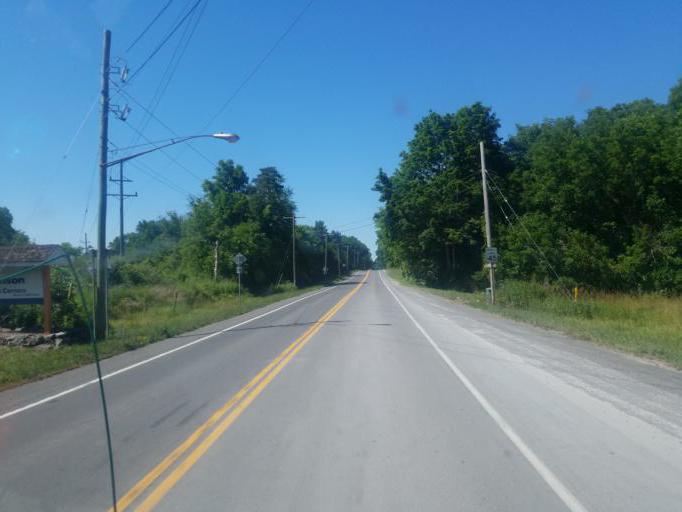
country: US
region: New York
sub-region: Ontario County
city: Phelps
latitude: 42.9340
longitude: -77.0128
